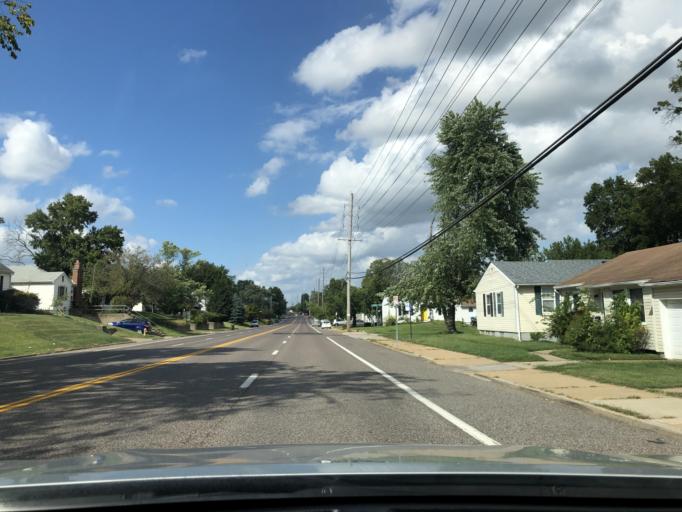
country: US
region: Missouri
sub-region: Saint Louis County
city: Affton
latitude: 38.5449
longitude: -90.3234
